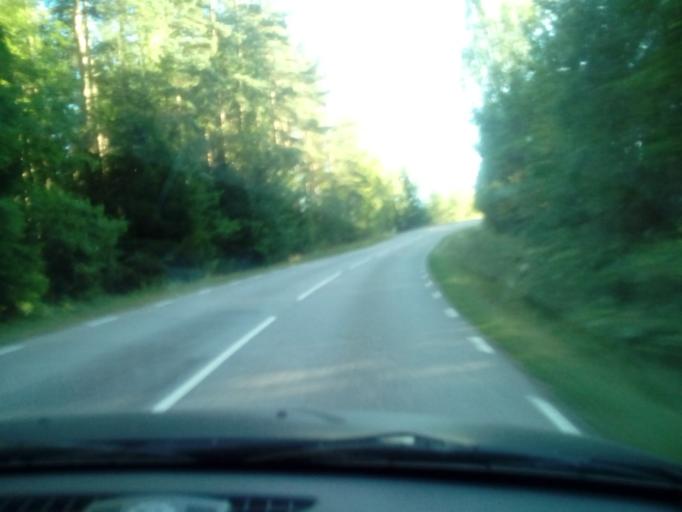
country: SE
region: Kalmar
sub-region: Vasterviks Kommun
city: Gamleby
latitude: 57.8080
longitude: 16.4340
